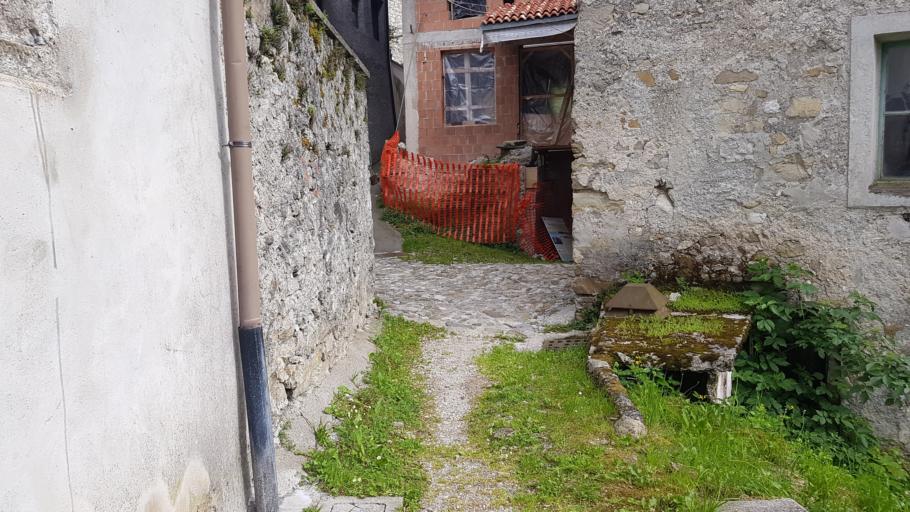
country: IT
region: Friuli Venezia Giulia
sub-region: Provincia di Udine
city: Moggio Udinese
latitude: 46.4684
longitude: 13.1933
